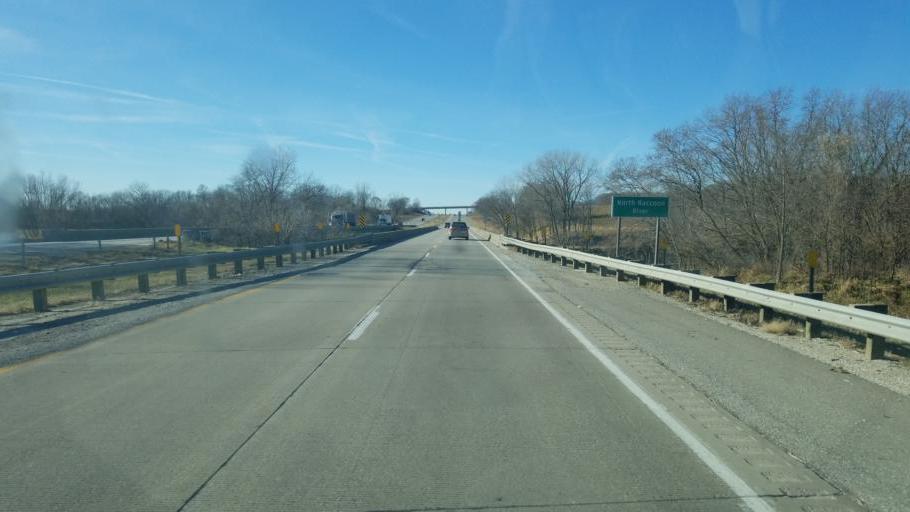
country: US
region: Iowa
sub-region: Dallas County
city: Van Meter
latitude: 41.5455
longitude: -93.9657
